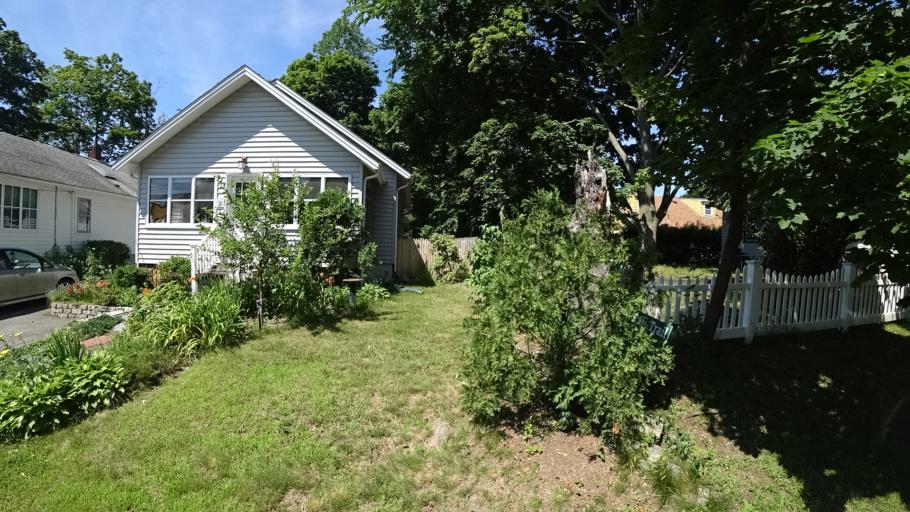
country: US
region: Massachusetts
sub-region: Norfolk County
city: Dedham
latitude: 42.2455
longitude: -71.1655
